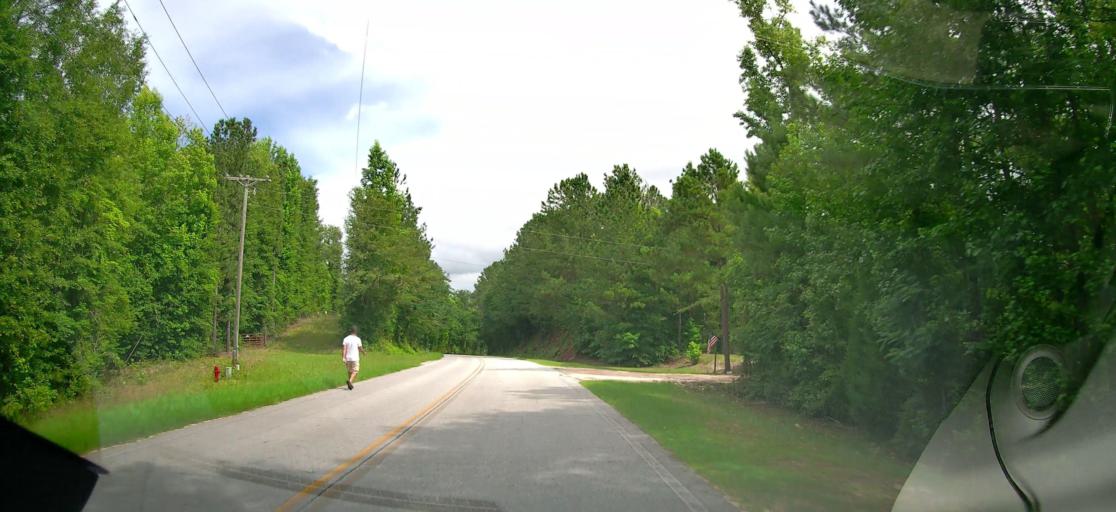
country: US
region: Georgia
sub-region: Peach County
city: Byron
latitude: 32.7124
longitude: -83.7802
